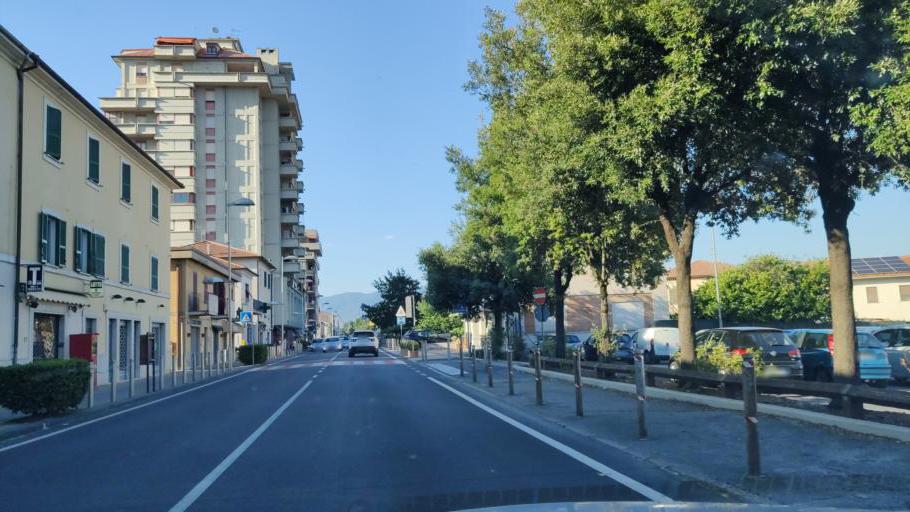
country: IT
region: Umbria
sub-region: Provincia di Terni
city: Narni Scalo
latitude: 42.5341
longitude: 12.5189
